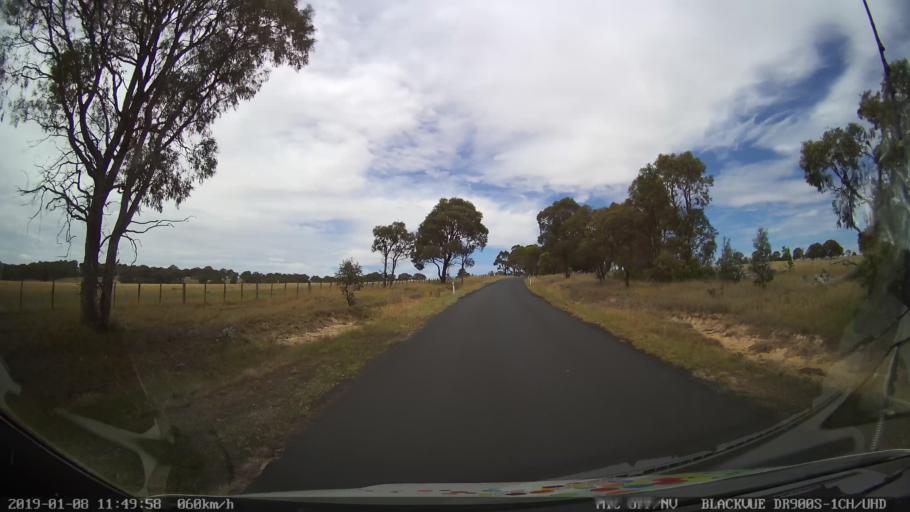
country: AU
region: New South Wales
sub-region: Armidale Dumaresq
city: Armidale
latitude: -30.3785
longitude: 151.5585
